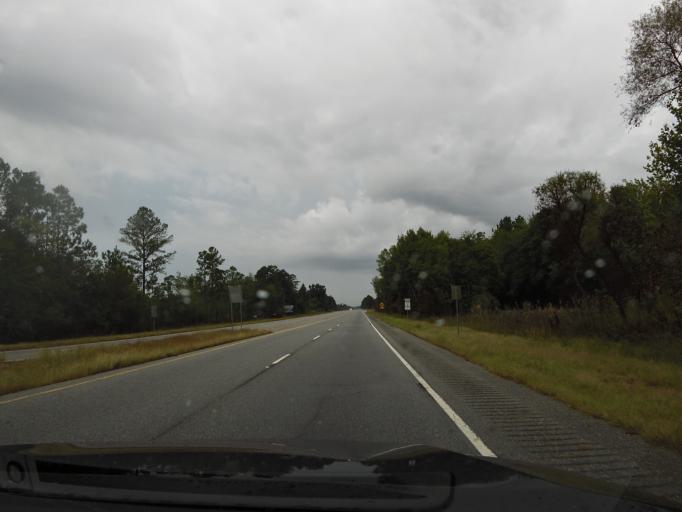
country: US
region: Georgia
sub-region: Wayne County
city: Jesup
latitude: 31.5350
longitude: -81.7948
